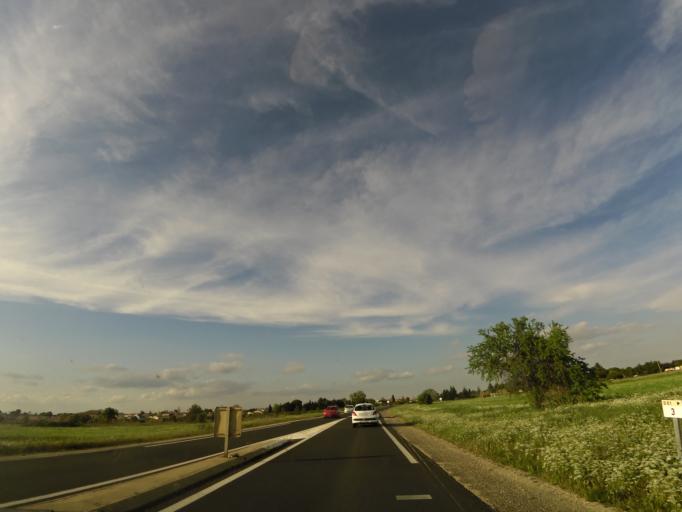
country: FR
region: Languedoc-Roussillon
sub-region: Departement de l'Herault
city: Lunel
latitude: 43.6625
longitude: 4.1386
